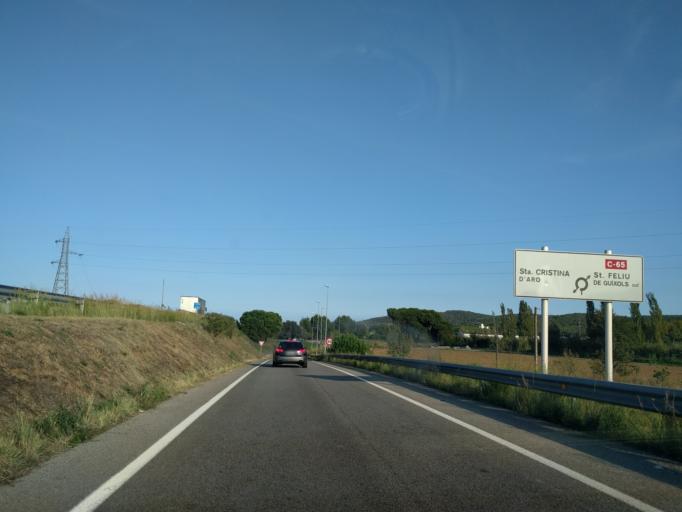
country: ES
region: Catalonia
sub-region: Provincia de Girona
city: Santa Cristina d'Aro
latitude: 41.8085
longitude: 3.0014
